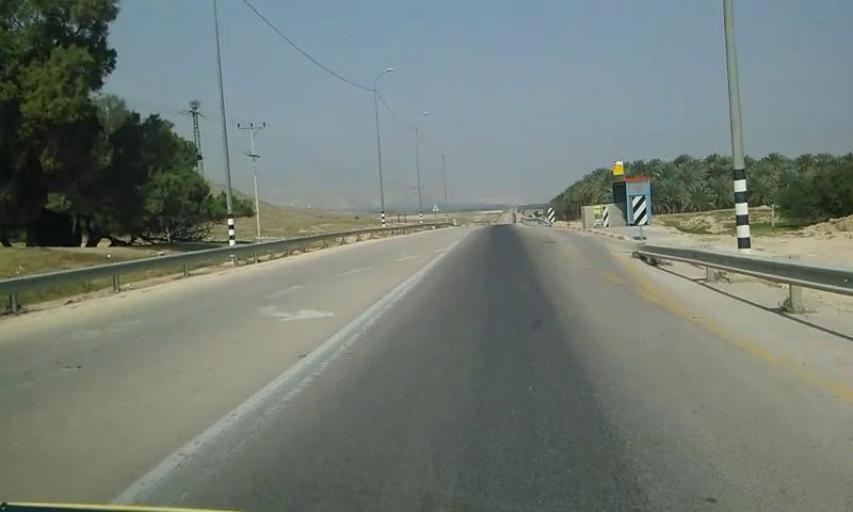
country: PS
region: West Bank
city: Al `Awja
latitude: 31.9775
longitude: 35.4675
